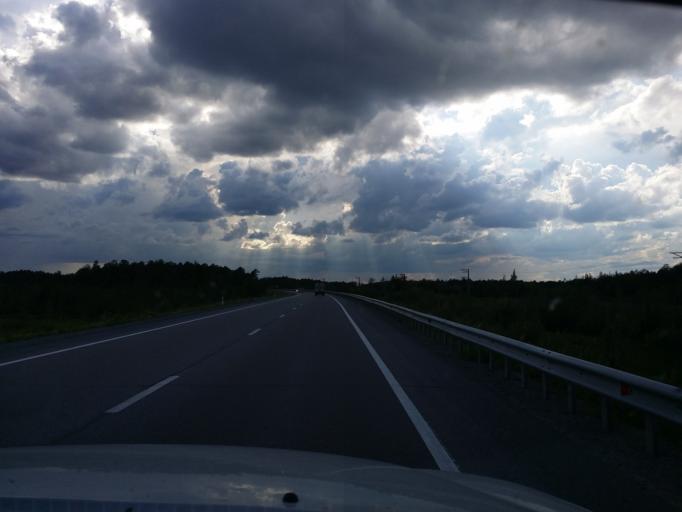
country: RU
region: Khanty-Mansiyskiy Avtonomnyy Okrug
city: Surgut
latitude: 61.4499
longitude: 74.0078
